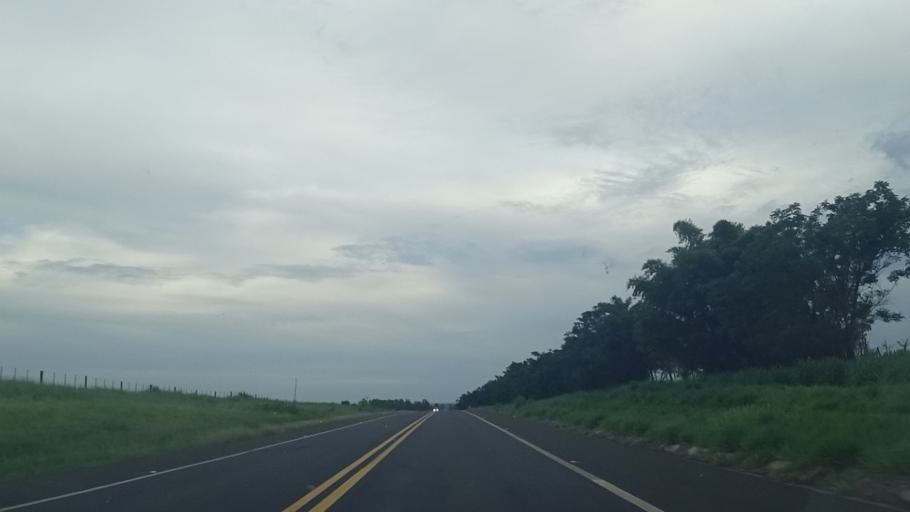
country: BR
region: Sao Paulo
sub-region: Martinopolis
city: Martinopolis
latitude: -22.0887
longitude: -51.1297
